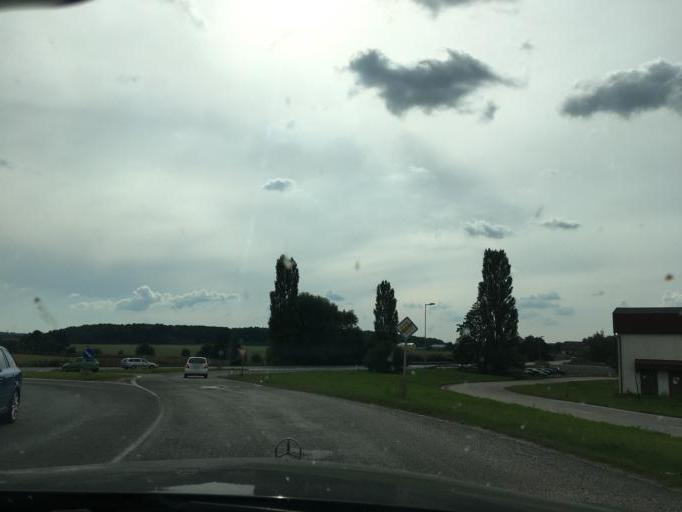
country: CZ
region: Kralovehradecky
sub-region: Okres Nachod
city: Nachod
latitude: 50.3984
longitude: 16.1050
